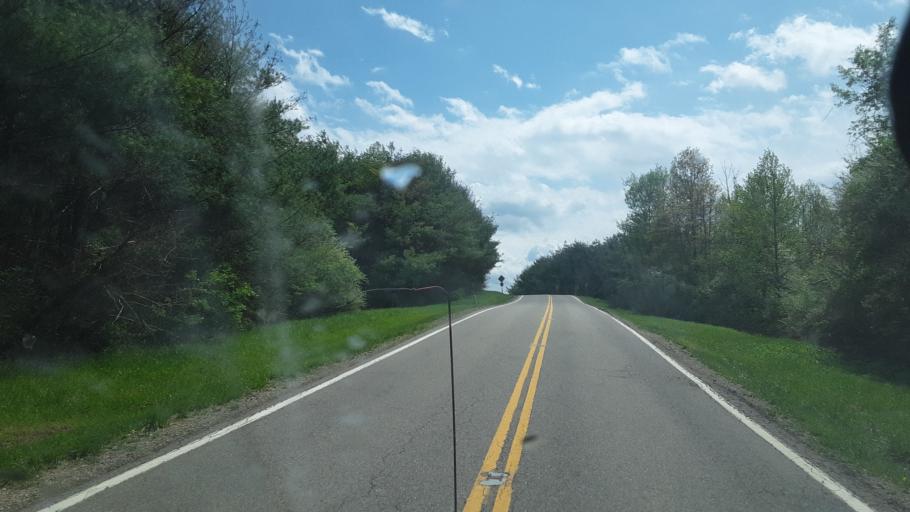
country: US
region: Ohio
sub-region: Noble County
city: Caldwell
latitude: 39.7286
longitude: -81.6523
